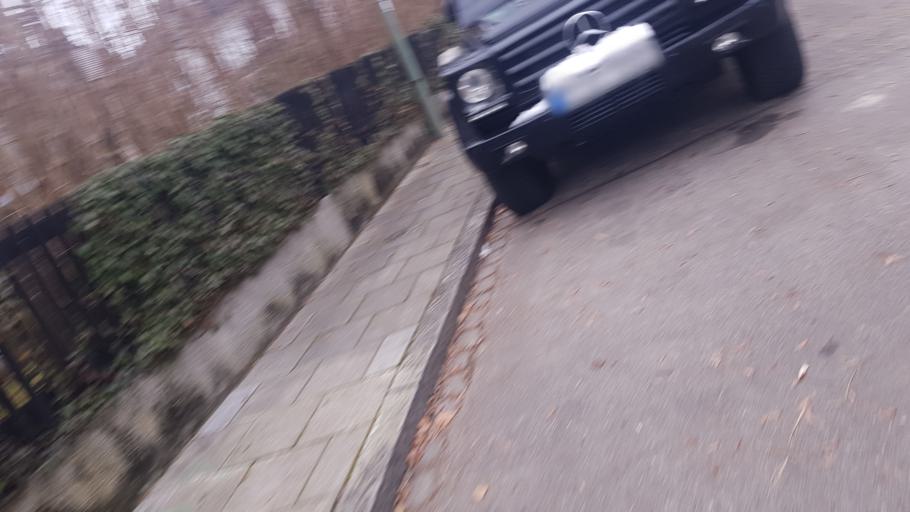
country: DE
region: Bavaria
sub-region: Upper Bavaria
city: Munich
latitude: 48.1613
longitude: 11.5173
